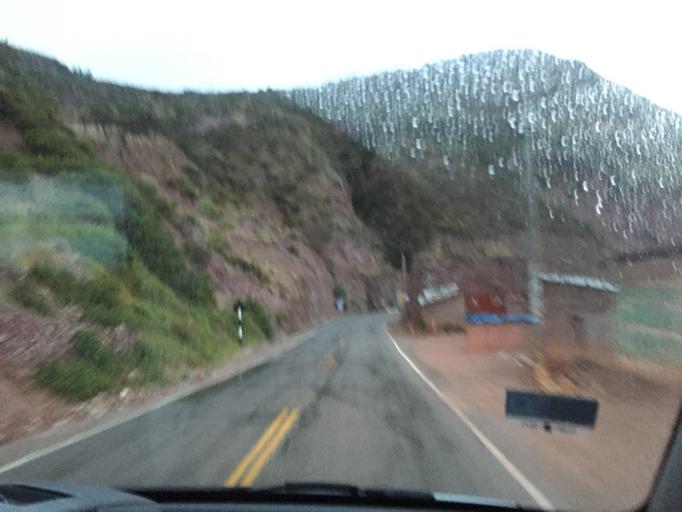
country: PE
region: Cusco
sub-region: Provincia de Urubamba
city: Urubamba
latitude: -13.3143
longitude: -72.1149
